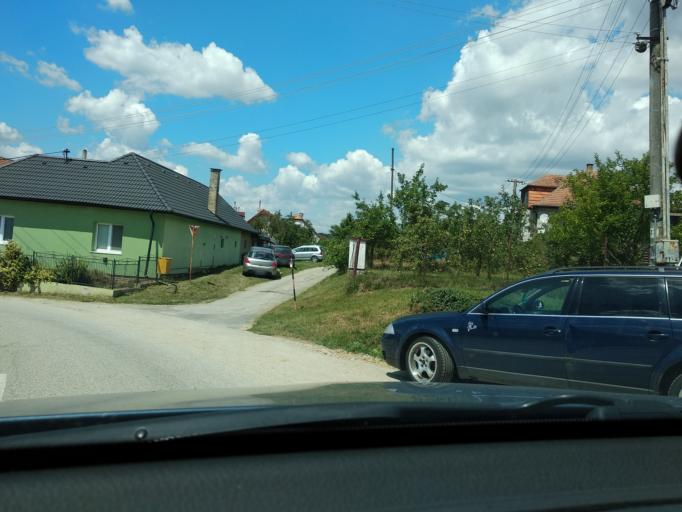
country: SK
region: Nitriansky
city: Banovce nad Bebravou
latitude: 48.7027
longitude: 18.1968
